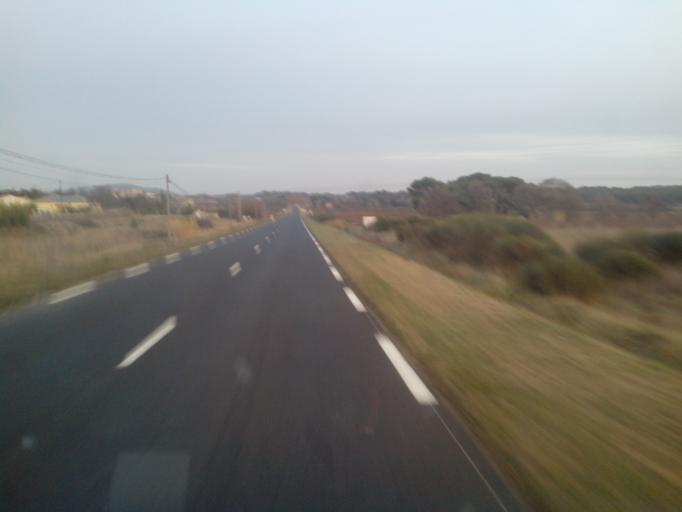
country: FR
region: Languedoc-Roussillon
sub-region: Departement de l'Aude
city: Ginestas
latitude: 43.2801
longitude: 2.8116
